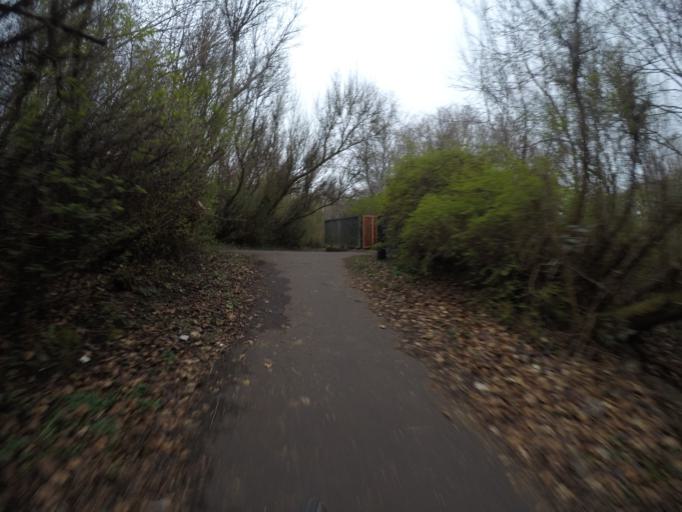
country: GB
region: Scotland
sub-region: North Ayrshire
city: Irvine
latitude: 55.6130
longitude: -4.6423
